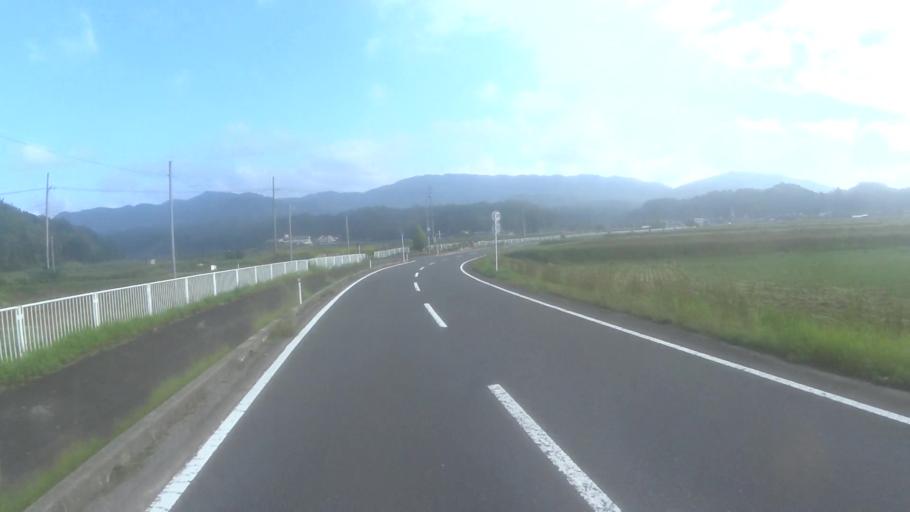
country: JP
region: Kyoto
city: Miyazu
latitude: 35.5954
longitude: 135.1343
